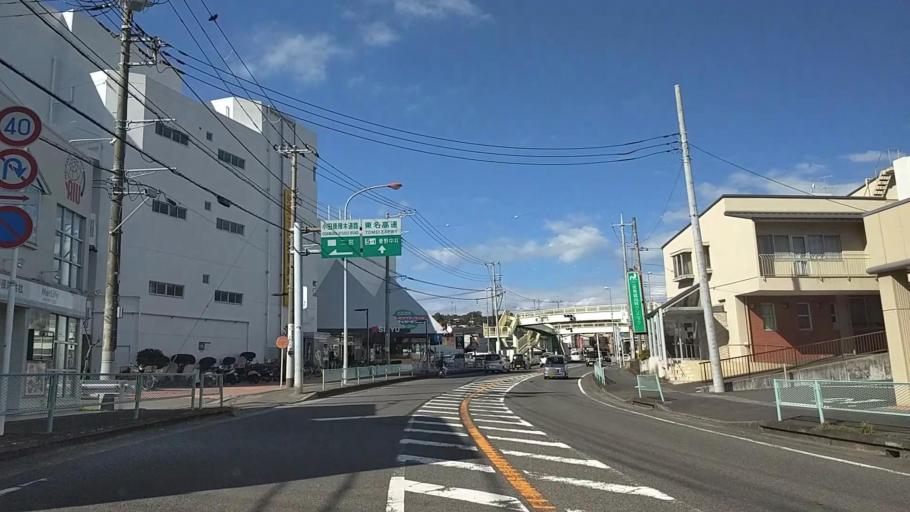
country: JP
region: Kanagawa
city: Ninomiya
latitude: 35.3088
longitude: 139.2479
